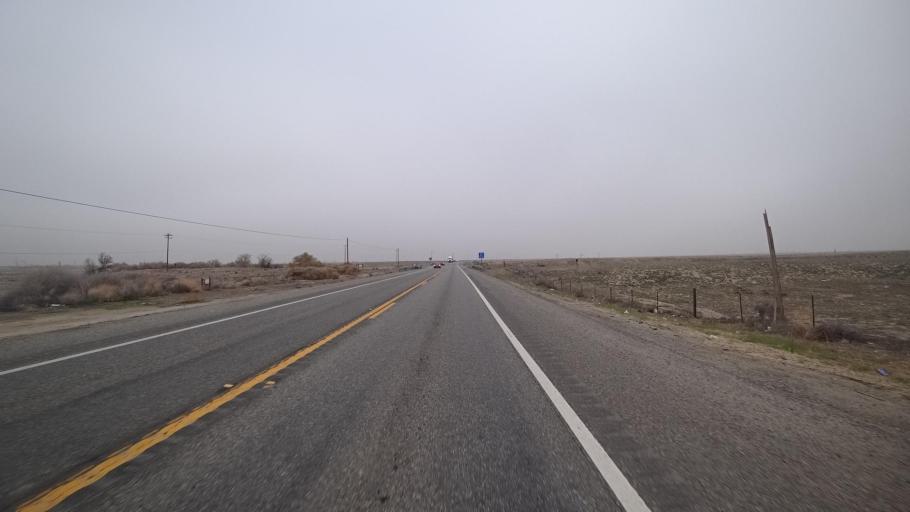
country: US
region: California
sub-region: Kern County
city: Ford City
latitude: 35.2667
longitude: -119.3084
